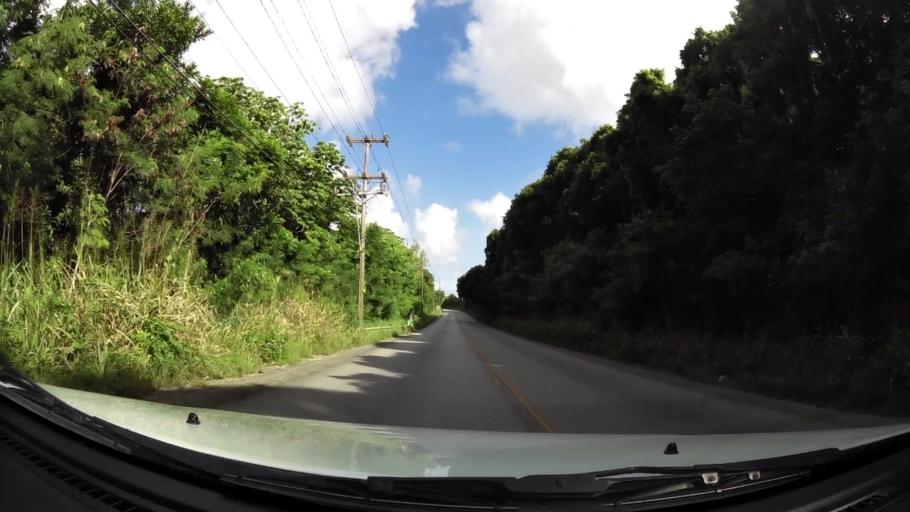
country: BB
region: Saint Peter
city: Speightstown
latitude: 13.2339
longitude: -59.6231
